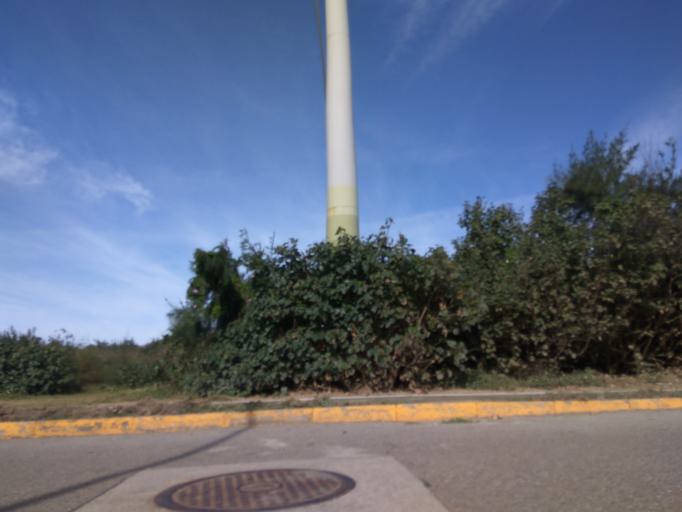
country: TW
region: Taiwan
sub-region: Hsinchu
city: Zhubei
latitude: 25.0425
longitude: 121.0702
